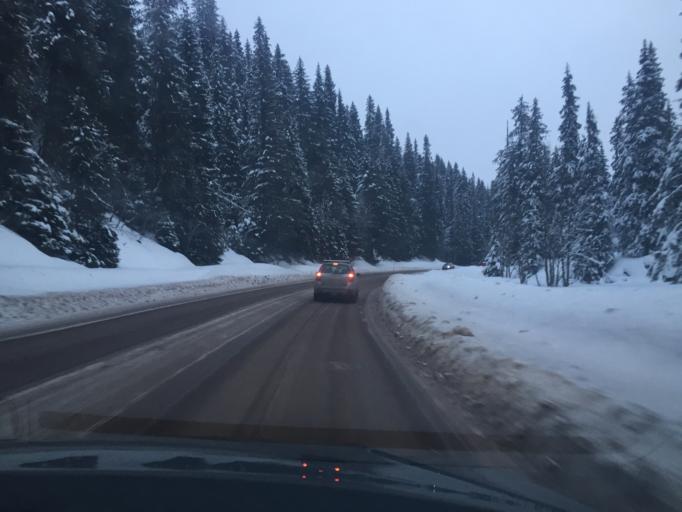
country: SE
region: Dalarna
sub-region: Malung-Saelens kommun
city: Malung
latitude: 61.1660
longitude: 13.1489
